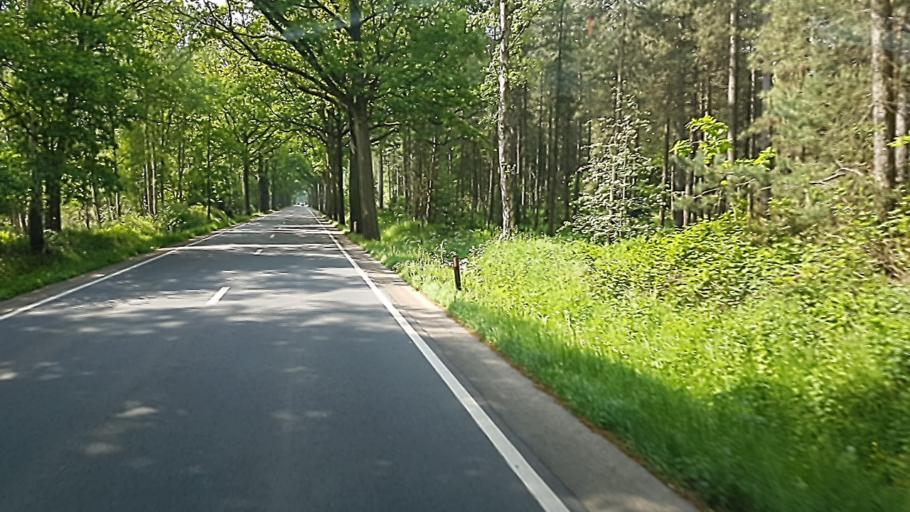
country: BE
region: Flanders
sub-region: Provincie Antwerpen
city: Kapellen
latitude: 51.3422
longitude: 4.4452
